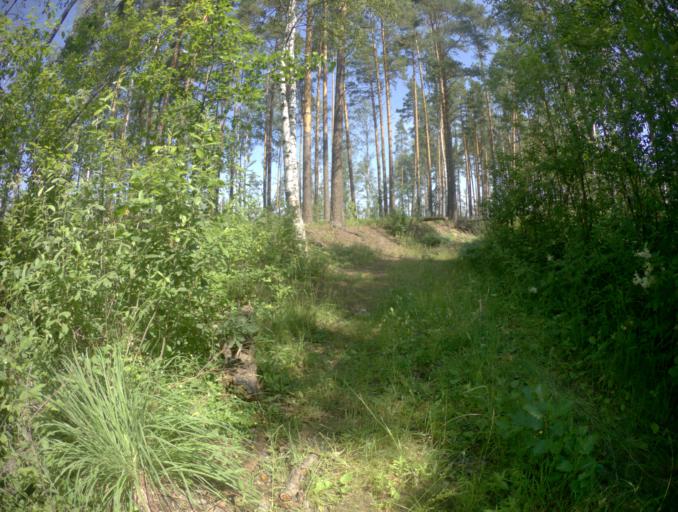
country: RU
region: Ivanovo
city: Talitsy
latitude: 56.4087
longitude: 42.2663
